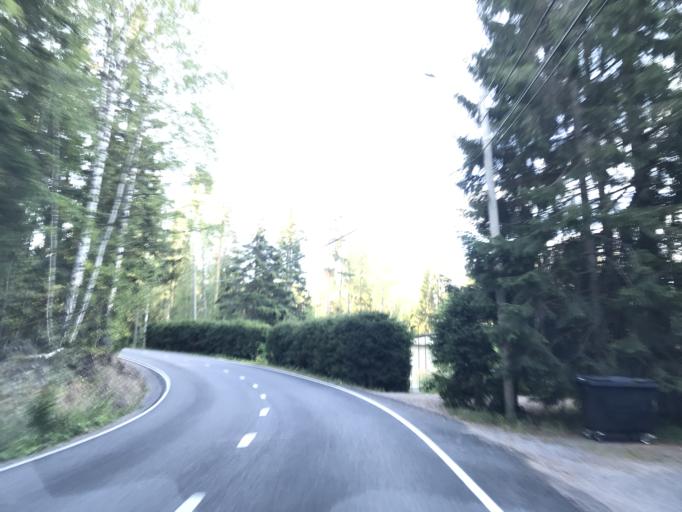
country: FI
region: Uusimaa
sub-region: Helsinki
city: Kauniainen
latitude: 60.3388
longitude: 24.7076
